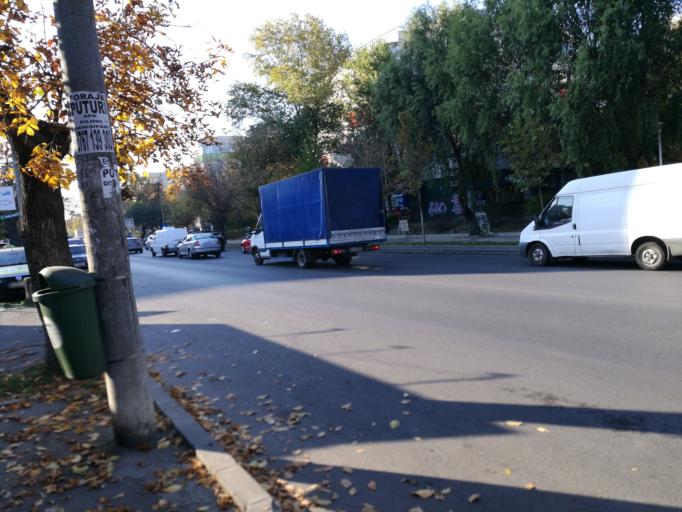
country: RO
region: Bucuresti
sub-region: Municipiul Bucuresti
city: Bucharest
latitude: 44.4791
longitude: 26.0954
